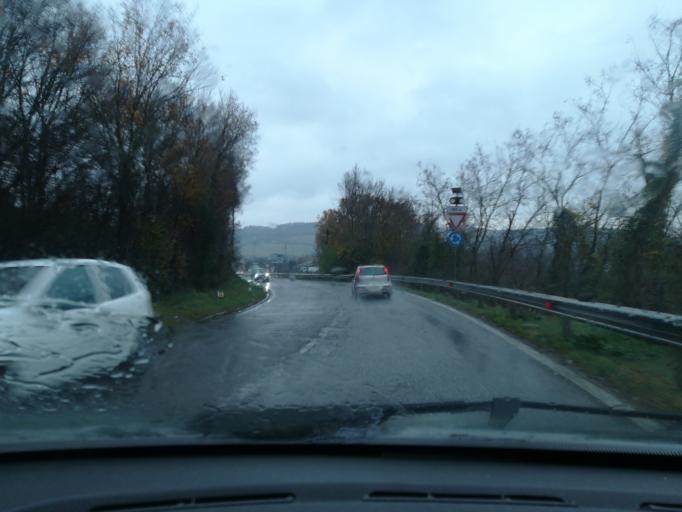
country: IT
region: The Marches
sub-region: Provincia di Macerata
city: Sforzacosta
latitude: 43.2615
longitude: 13.4217
